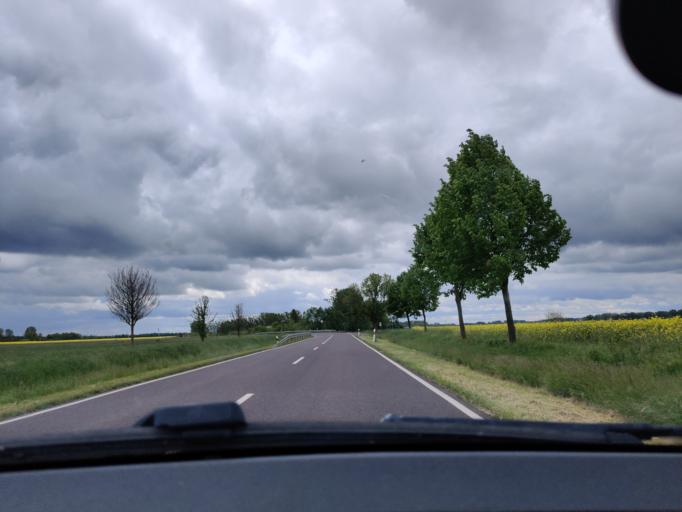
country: DE
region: Saxony-Anhalt
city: Schonebeck
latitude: 51.9836
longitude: 11.7622
